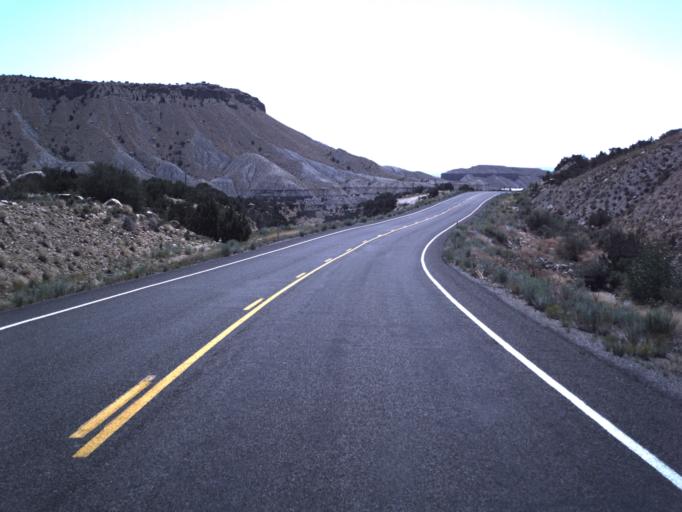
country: US
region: Utah
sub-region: Emery County
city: Orangeville
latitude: 39.2799
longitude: -111.1020
